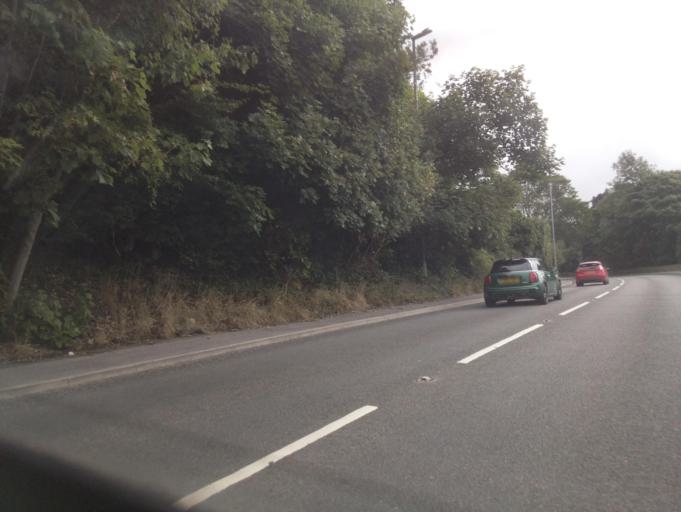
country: GB
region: England
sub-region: Kirklees
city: Holmfirth
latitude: 53.5735
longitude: -1.7465
